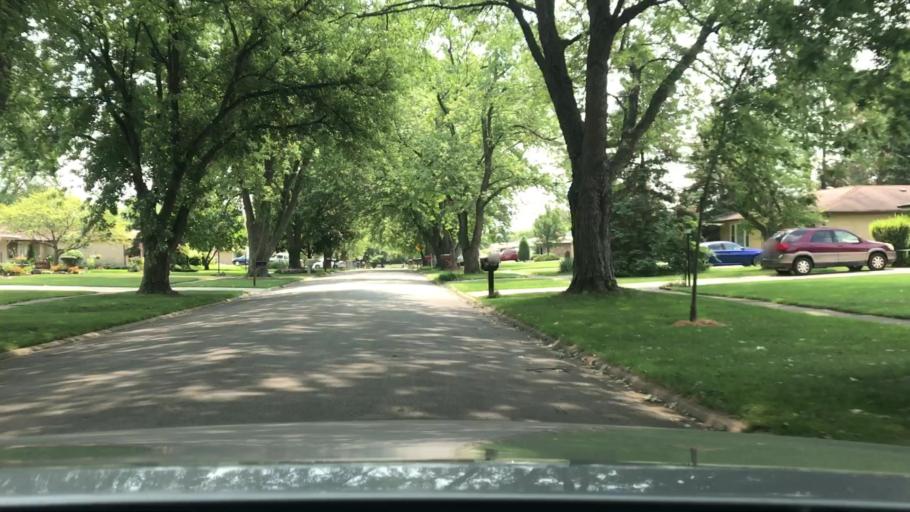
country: US
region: Illinois
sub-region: DuPage County
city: Darien
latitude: 41.7401
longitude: -87.9890
